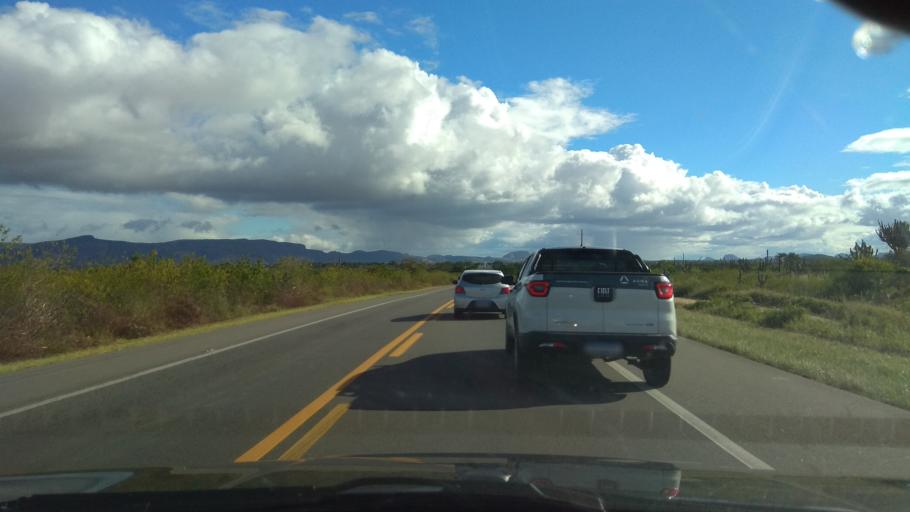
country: BR
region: Bahia
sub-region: Castro Alves
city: Castro Alves
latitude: -12.6743
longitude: -39.6578
